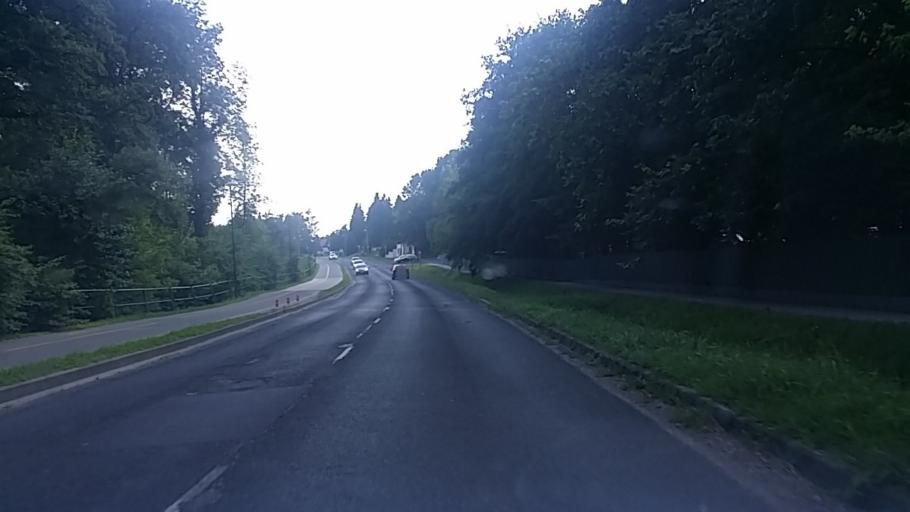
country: HU
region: Zala
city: Heviz
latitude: 46.7844
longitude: 17.1921
